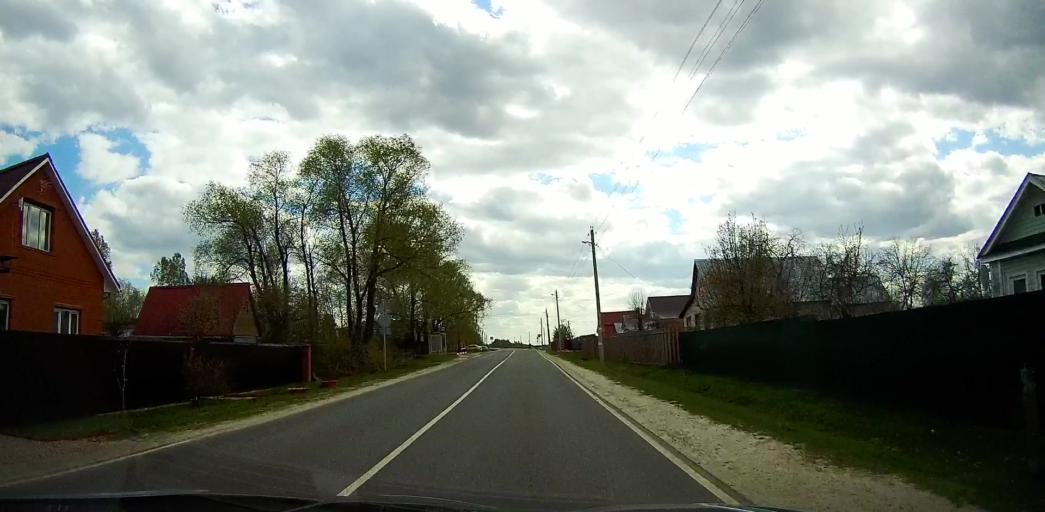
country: RU
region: Moskovskaya
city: Davydovo
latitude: 55.6446
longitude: 38.7508
